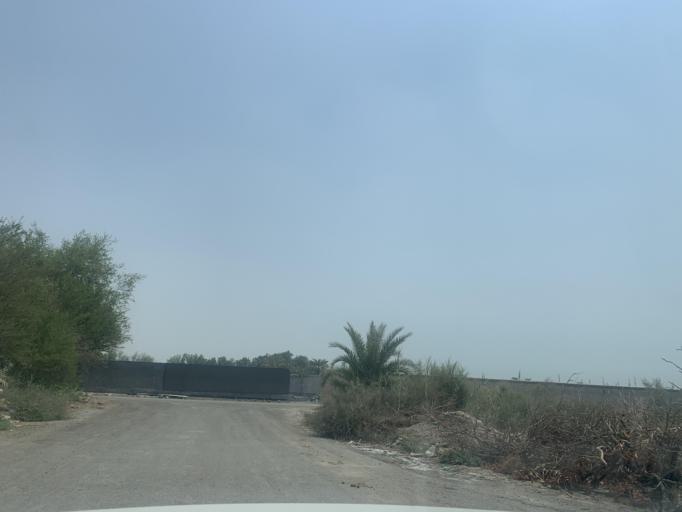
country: BH
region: Central Governorate
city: Madinat Hamad
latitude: 26.1244
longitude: 50.4693
